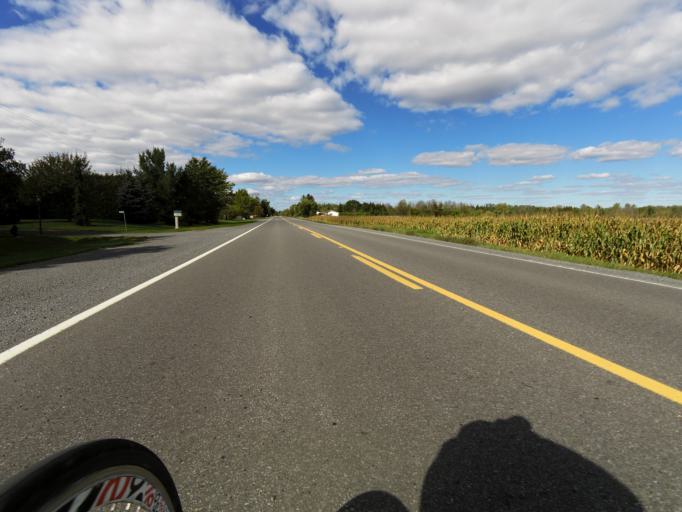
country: CA
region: Ontario
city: Bells Corners
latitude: 45.1652
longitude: -75.6562
